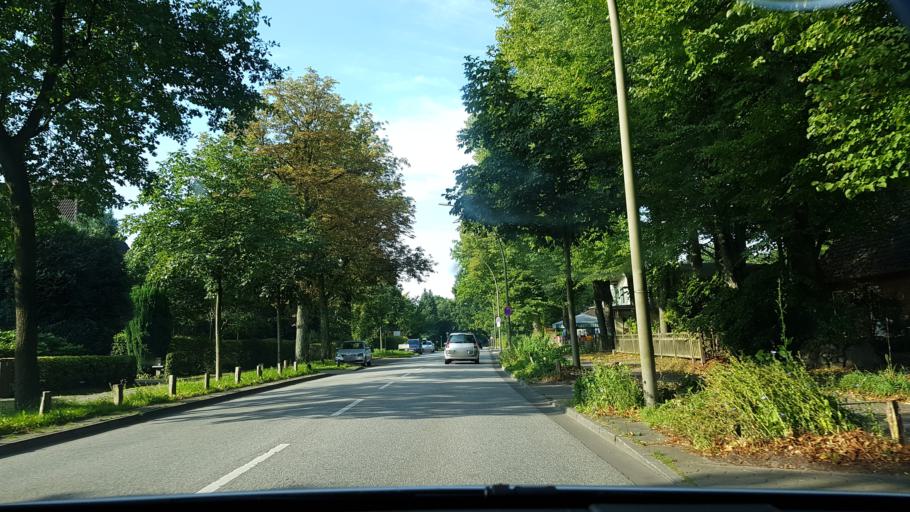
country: DE
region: Hamburg
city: Farmsen-Berne
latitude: 53.6352
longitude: 10.1482
